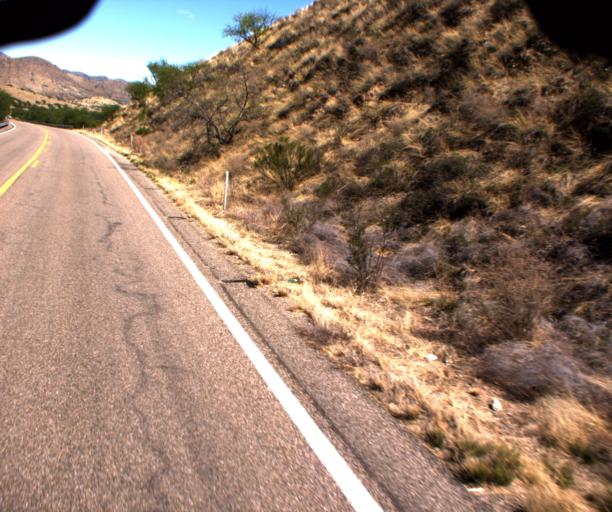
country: US
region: Arizona
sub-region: Santa Cruz County
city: Rio Rico
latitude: 31.4692
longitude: -110.8209
